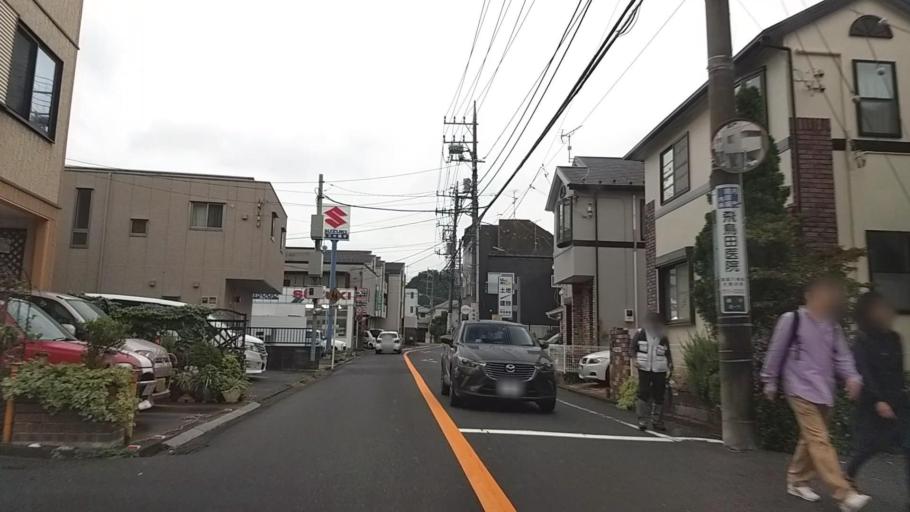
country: JP
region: Kanagawa
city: Yokohama
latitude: 35.4095
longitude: 139.6207
